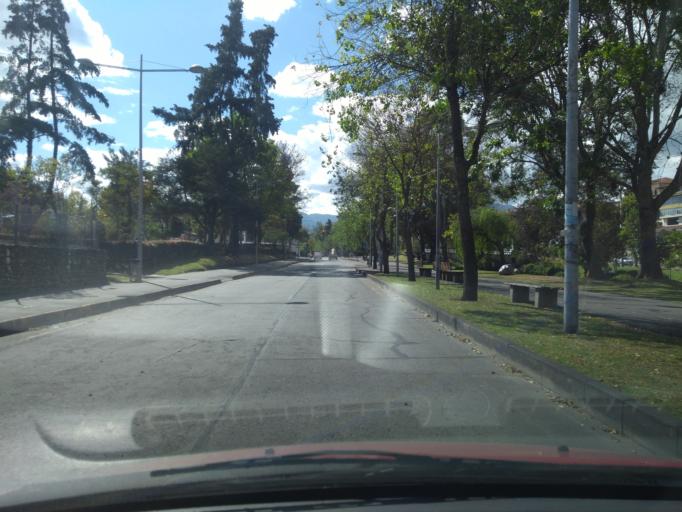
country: EC
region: Azuay
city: Cuenca
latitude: -2.9041
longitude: -79.0026
